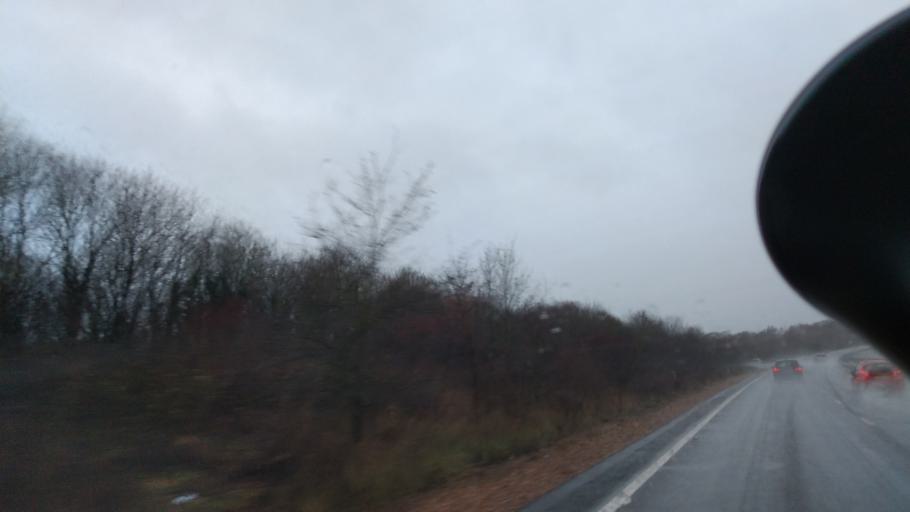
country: GB
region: England
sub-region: West Sussex
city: Goring-by-Sea
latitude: 50.8385
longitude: -0.4553
